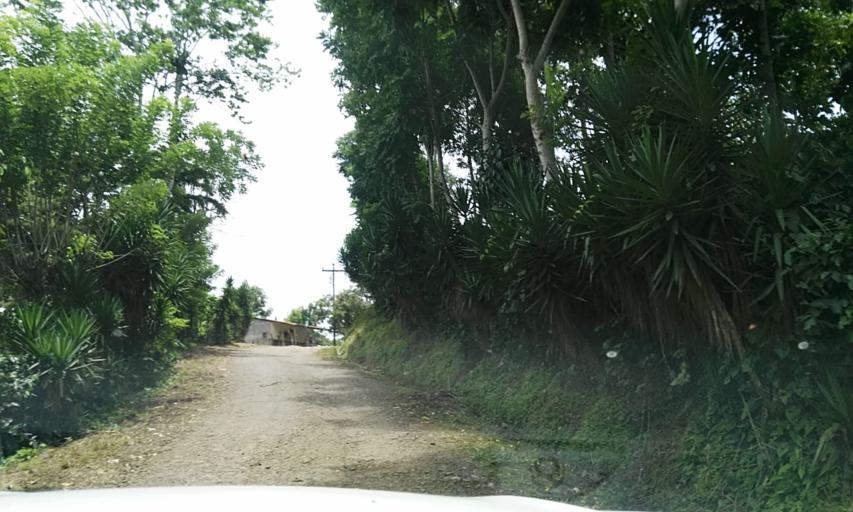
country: NI
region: Matagalpa
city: San Ramon
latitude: 13.0062
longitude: -85.8720
